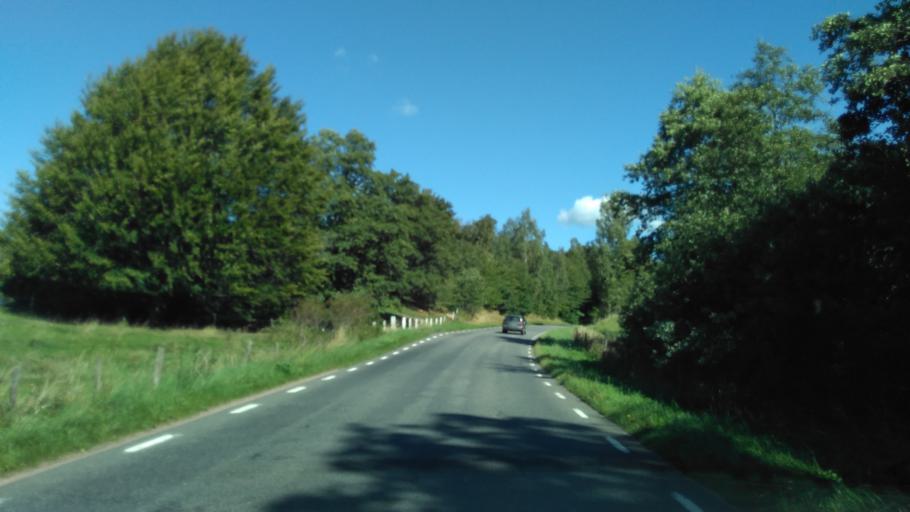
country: SE
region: Vaestra Goetaland
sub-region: Skara Kommun
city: Axvall
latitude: 58.4371
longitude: 13.6494
